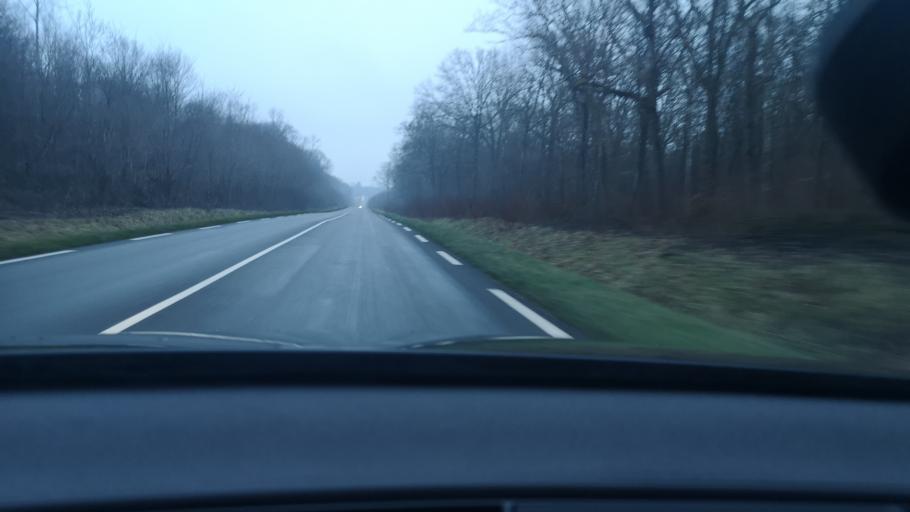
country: FR
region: Bourgogne
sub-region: Departement de la Cote-d'Or
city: Fenay
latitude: 47.1622
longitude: 5.0850
